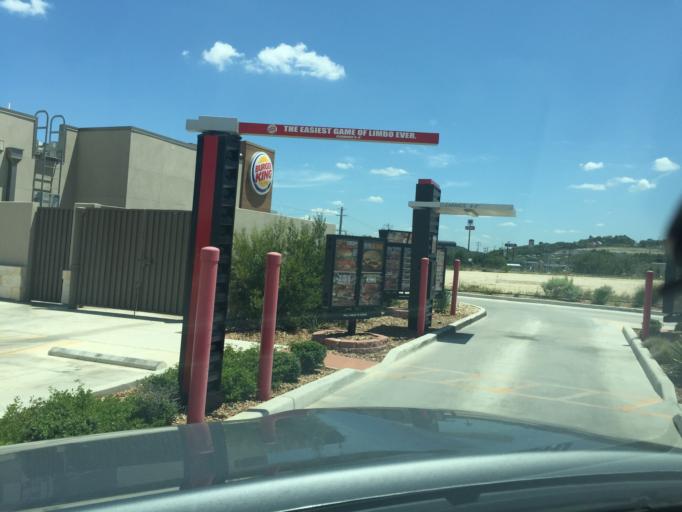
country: US
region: Texas
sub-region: Comal County
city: Bulverde
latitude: 29.8008
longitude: -98.4198
